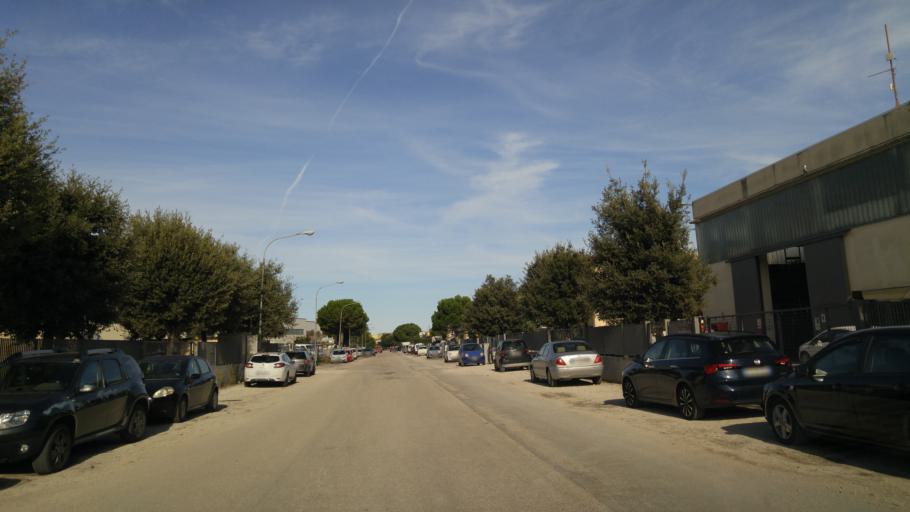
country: IT
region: The Marches
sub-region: Provincia di Pesaro e Urbino
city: Bellocchi
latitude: 43.7852
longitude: 13.0073
